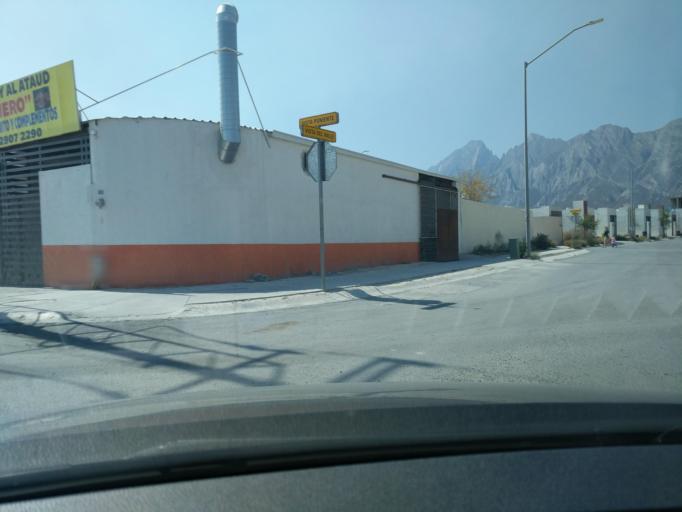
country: MX
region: Nuevo Leon
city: Garcia
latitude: 25.8192
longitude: -100.5377
